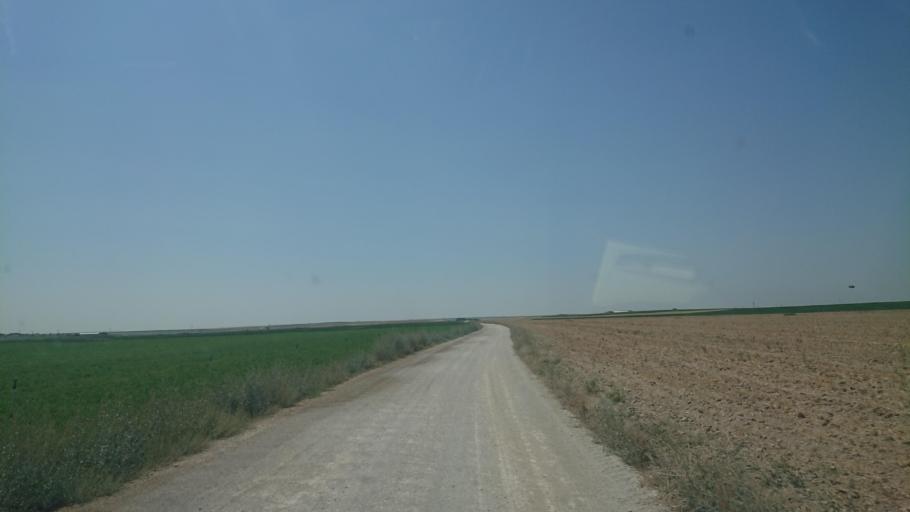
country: TR
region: Aksaray
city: Sultanhani
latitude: 38.2180
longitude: 33.6435
